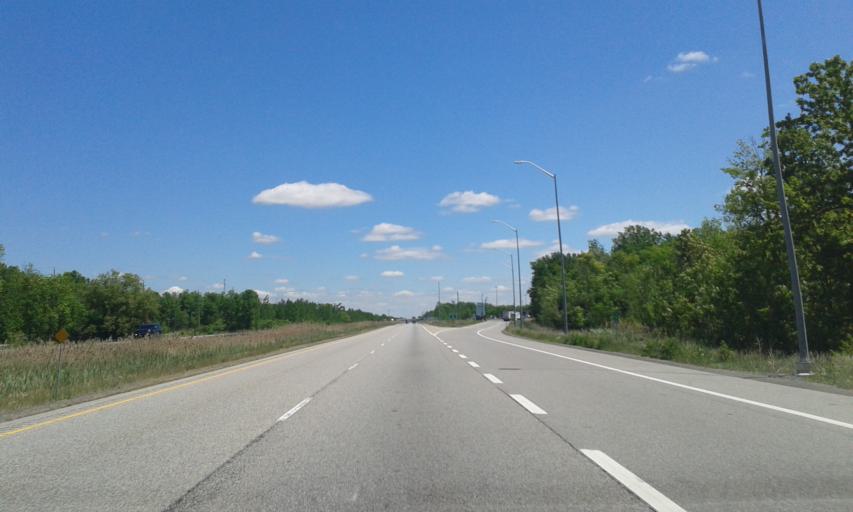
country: US
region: New York
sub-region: St. Lawrence County
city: Norfolk
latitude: 44.9428
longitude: -75.1357
